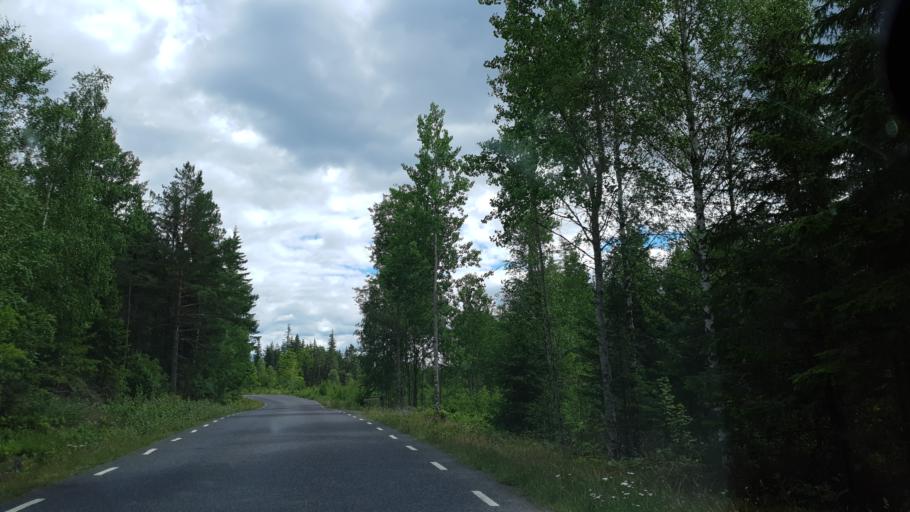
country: SE
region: Kronoberg
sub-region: Uppvidinge Kommun
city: Aseda
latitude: 57.1909
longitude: 15.4020
